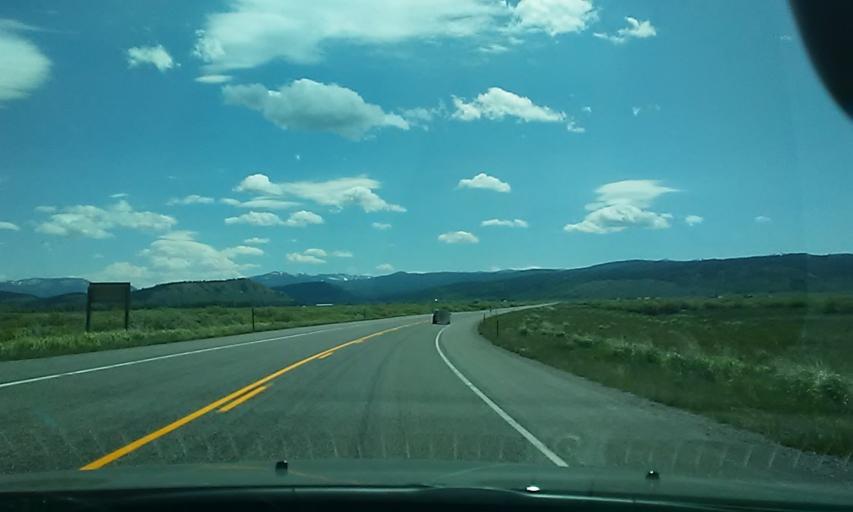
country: US
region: Wyoming
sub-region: Teton County
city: Jackson
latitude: 43.8380
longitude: -110.4386
